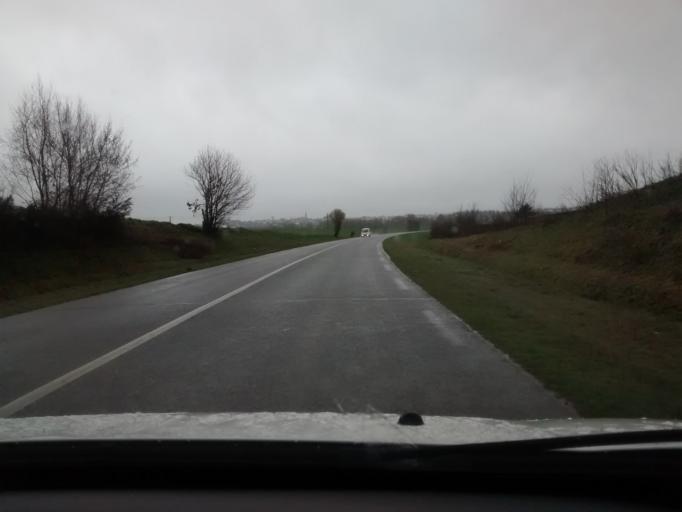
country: FR
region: Brittany
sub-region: Departement d'Ille-et-Vilaine
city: Acigne
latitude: 48.1359
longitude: -1.5167
